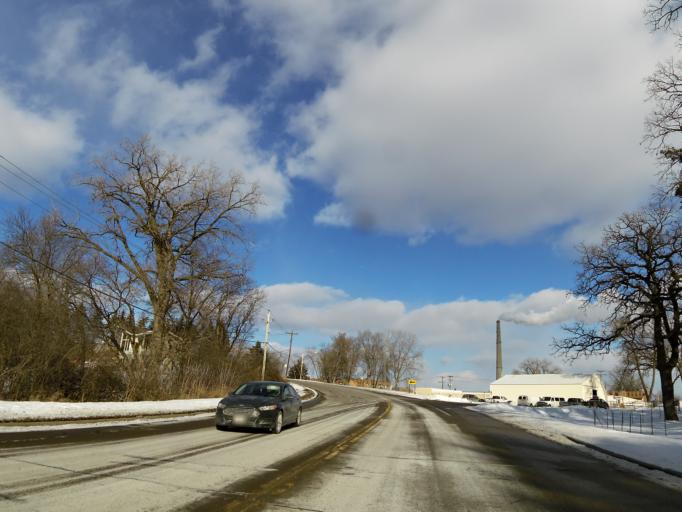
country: US
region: Minnesota
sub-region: Washington County
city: Oak Park Heights
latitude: 45.0246
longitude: -92.7930
